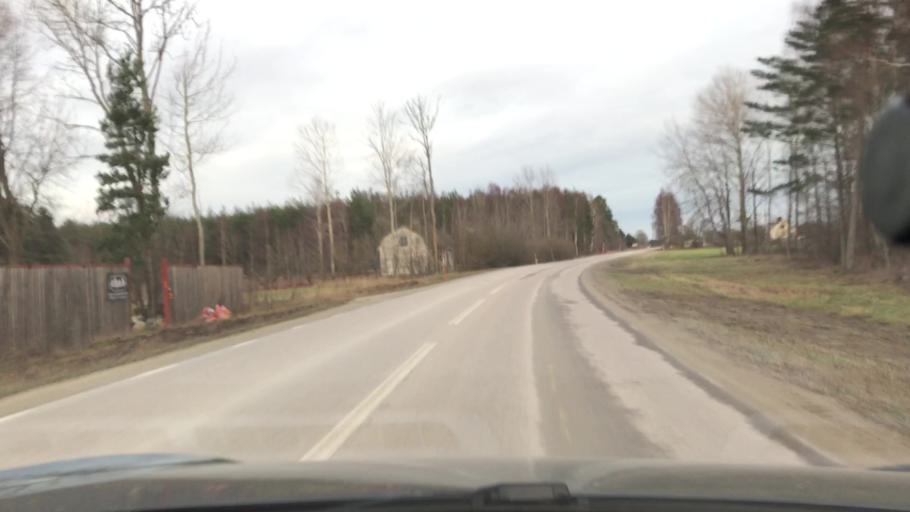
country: SE
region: Gotland
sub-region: Gotland
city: Slite
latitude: 57.7231
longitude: 18.5647
